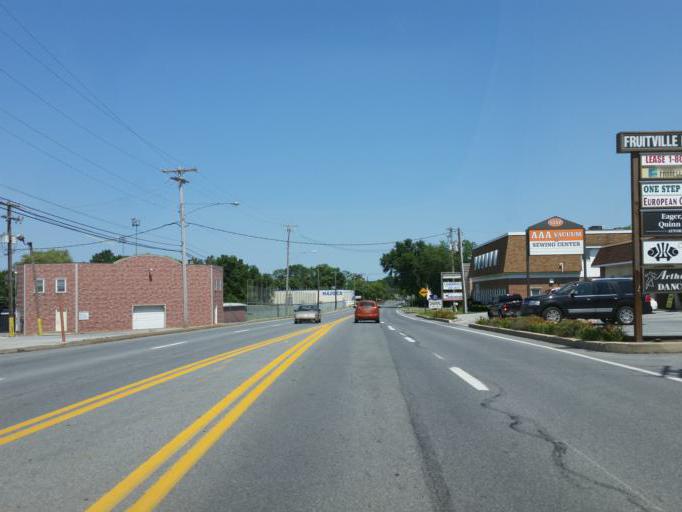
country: US
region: Pennsylvania
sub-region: Lancaster County
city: Lancaster
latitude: 40.0577
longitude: -76.3116
